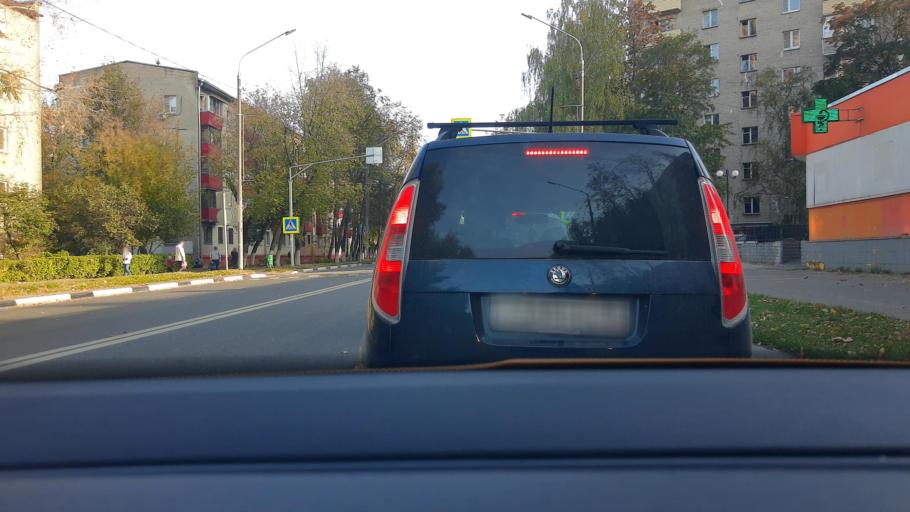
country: RU
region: Moskovskaya
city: Reutov
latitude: 55.7633
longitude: 37.8550
